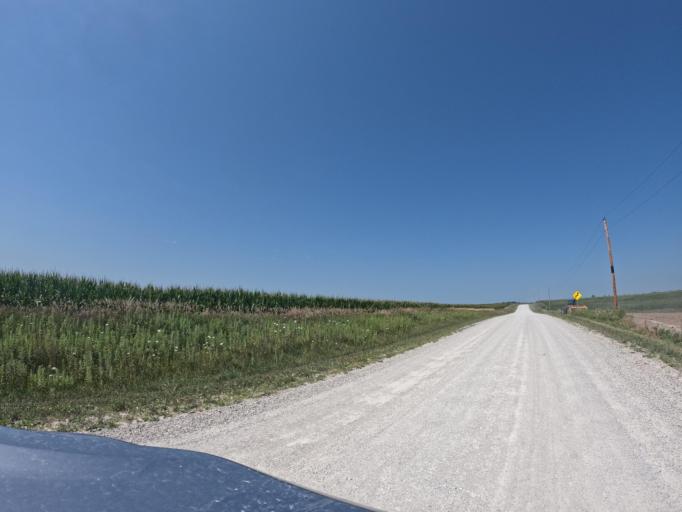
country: US
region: Iowa
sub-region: Henry County
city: Mount Pleasant
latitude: 40.8874
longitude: -91.5706
